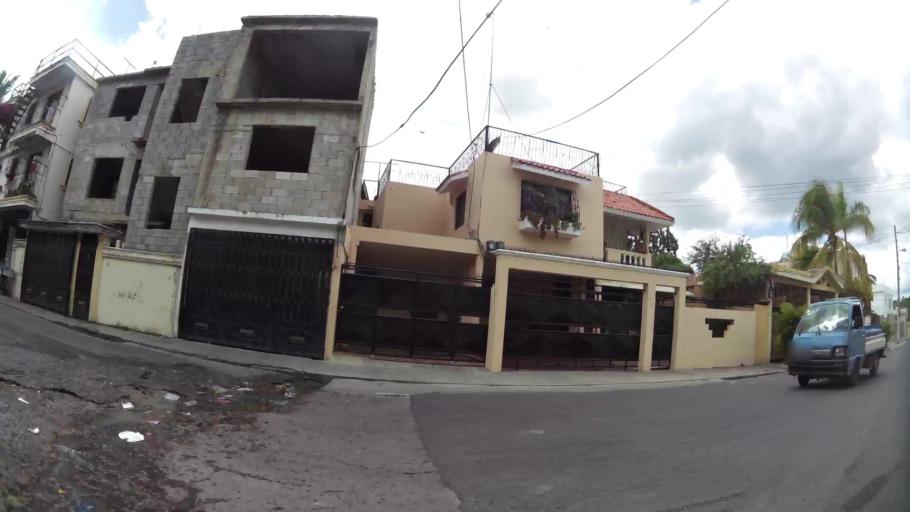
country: DO
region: Nacional
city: Ensanche Luperon
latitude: 18.5201
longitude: -69.9090
